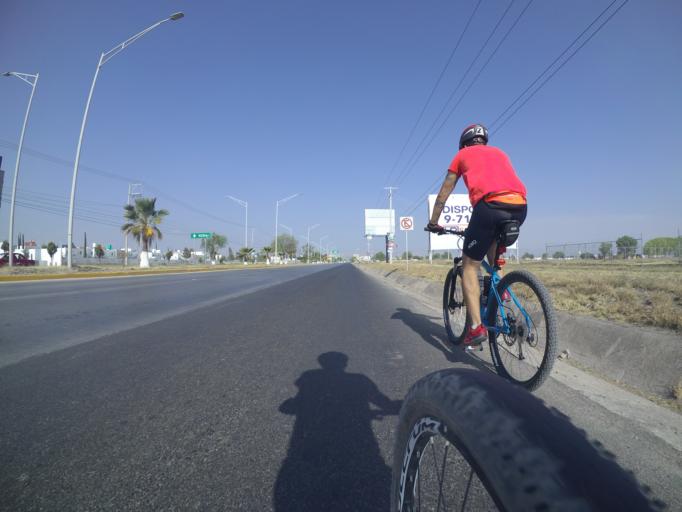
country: MX
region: Aguascalientes
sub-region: Jesus Maria
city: Arboledas Paso Blanco [Fraccionamiento]
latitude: 21.9474
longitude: -102.3055
